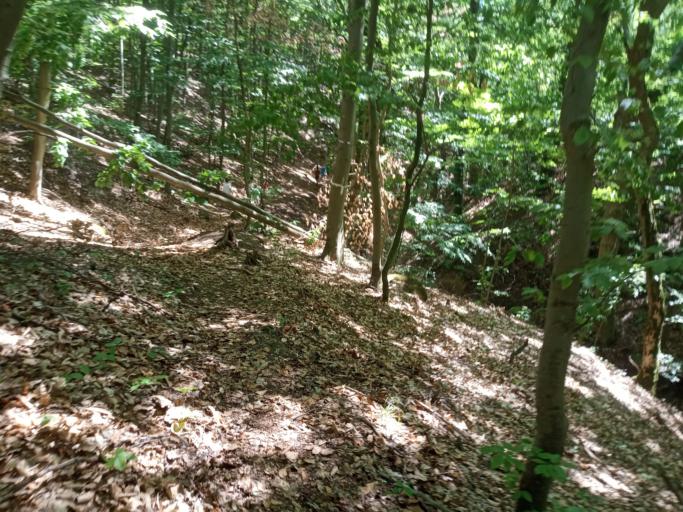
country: HU
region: Nograd
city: Matraverebely
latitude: 48.0050
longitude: 19.7591
